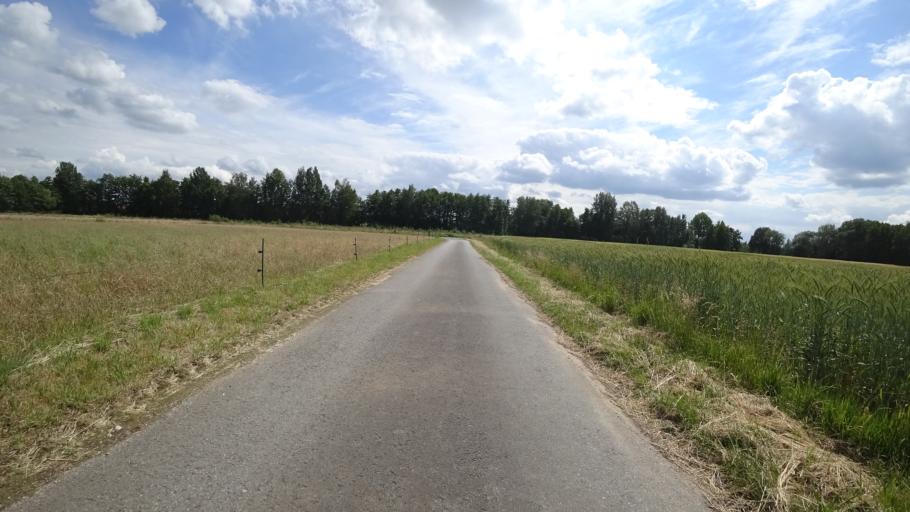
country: DE
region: North Rhine-Westphalia
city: Rietberg
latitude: 51.8134
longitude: 8.4158
